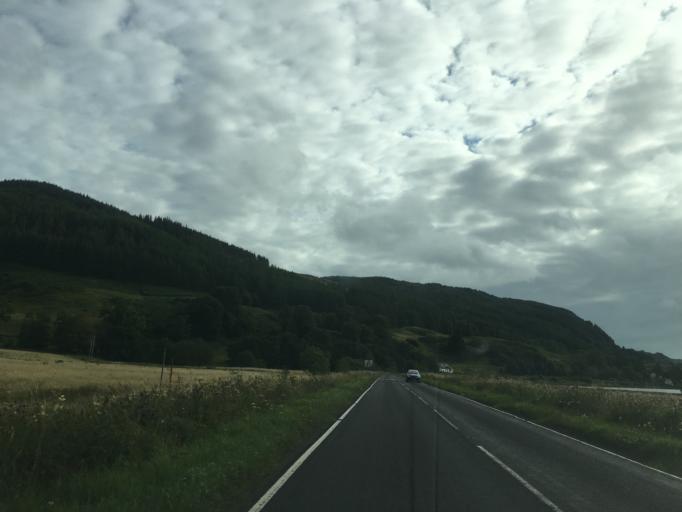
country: GB
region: Scotland
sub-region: Argyll and Bute
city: Oban
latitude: 56.3649
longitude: -5.4407
